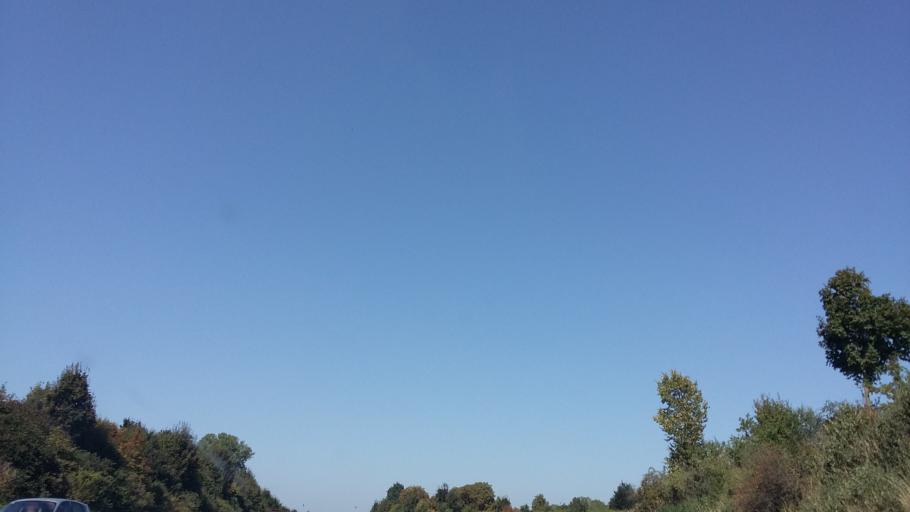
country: DE
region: Bavaria
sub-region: Swabia
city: Klosterlechfeld
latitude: 48.1587
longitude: 10.8404
